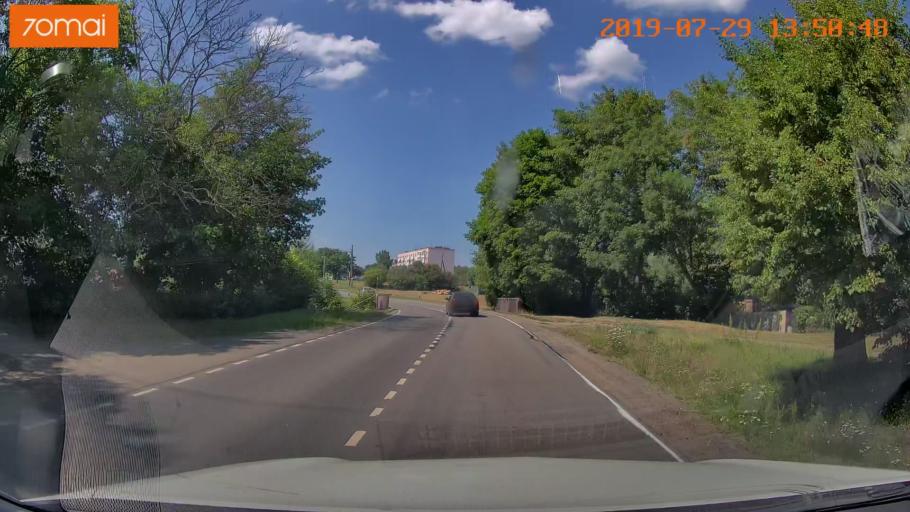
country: RU
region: Kaliningrad
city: Primorsk
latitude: 54.7287
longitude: 20.0095
